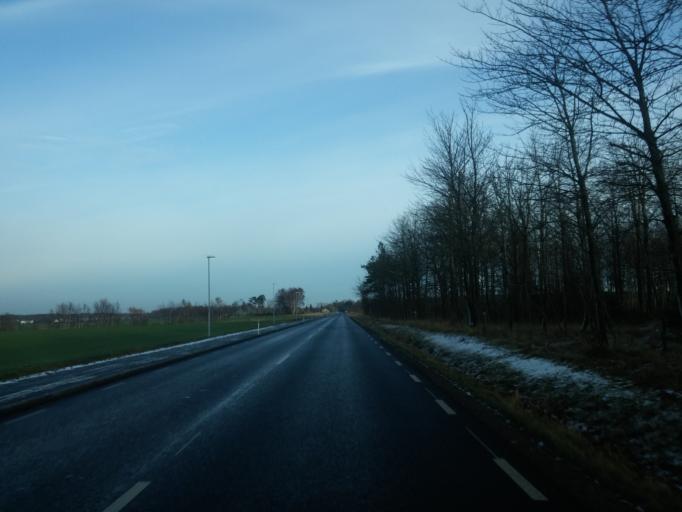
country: SE
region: Skane
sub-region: Angelholms Kommun
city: AEngelholm
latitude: 56.2198
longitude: 12.8200
